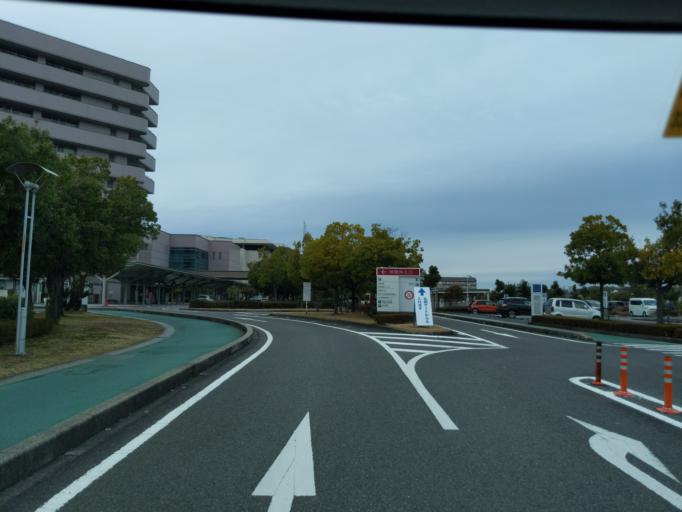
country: JP
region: Aichi
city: Kasugai
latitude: 35.2707
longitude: 136.9703
